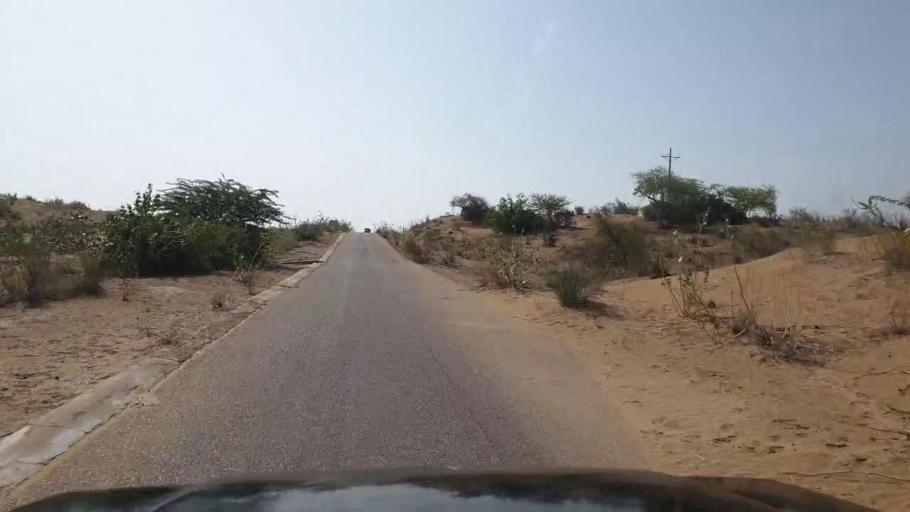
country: PK
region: Sindh
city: Mithi
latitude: 24.9756
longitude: 70.0058
